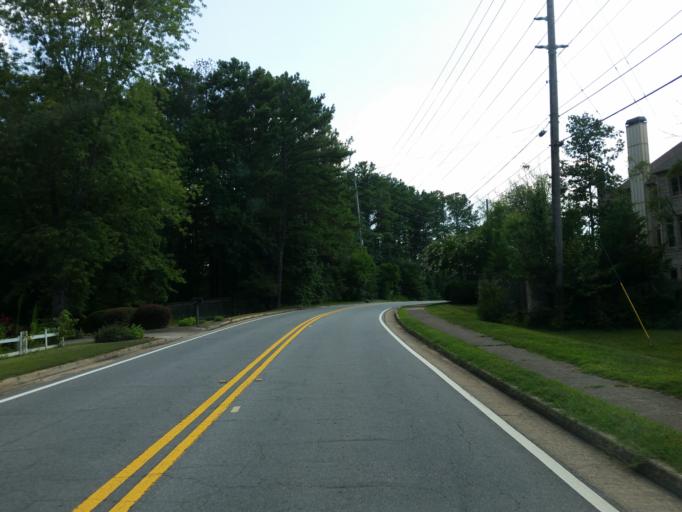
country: US
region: Georgia
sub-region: Fulton County
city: Roswell
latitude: 34.0142
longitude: -84.4581
